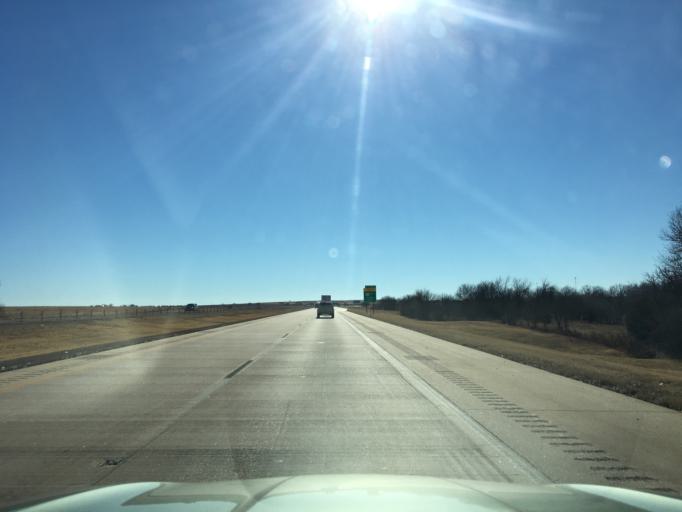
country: US
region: Oklahoma
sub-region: Noble County
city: Perry
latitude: 36.4204
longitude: -97.3271
